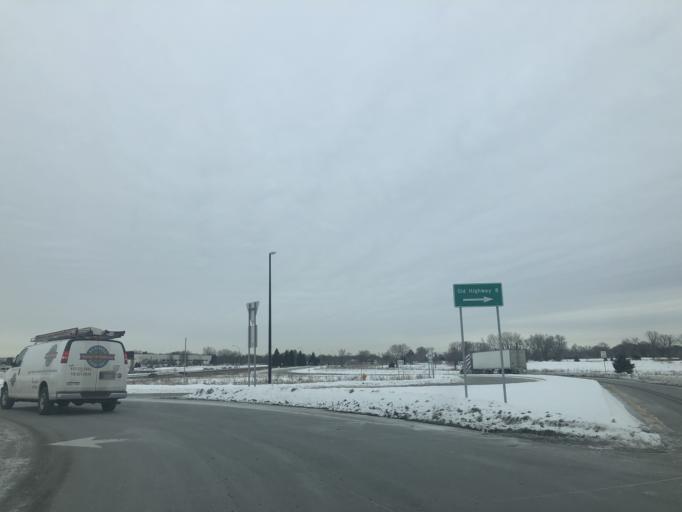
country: US
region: Minnesota
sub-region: Ramsey County
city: Mounds View
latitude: 45.0954
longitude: -93.1865
